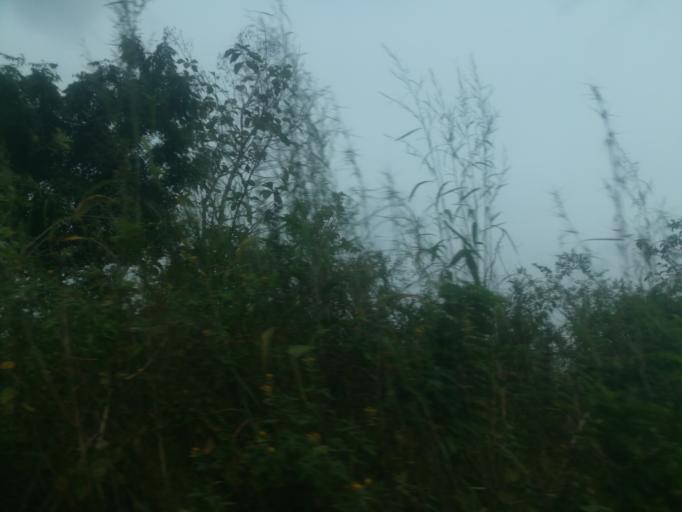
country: NG
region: Ogun
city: Ayetoro
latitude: 7.3514
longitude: 3.0534
